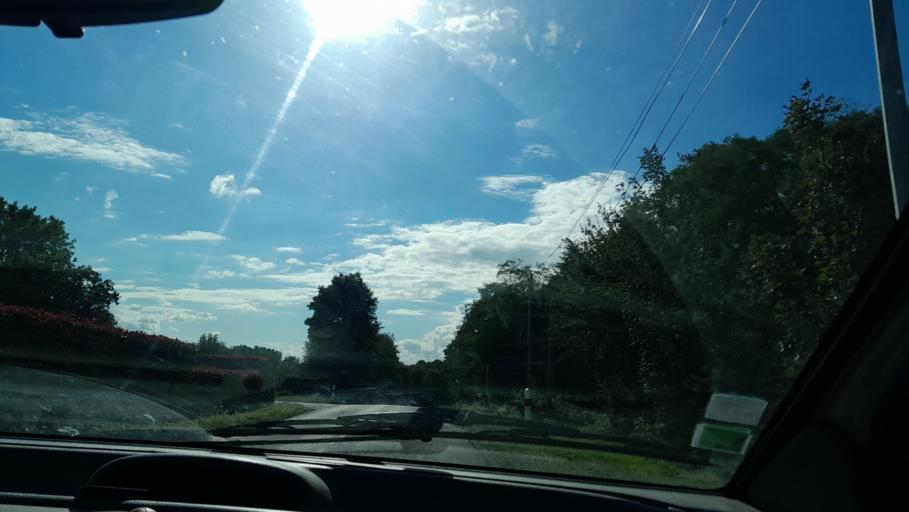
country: FR
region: Pays de la Loire
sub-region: Departement de la Mayenne
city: Ahuille
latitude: 48.0279
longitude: -0.8545
